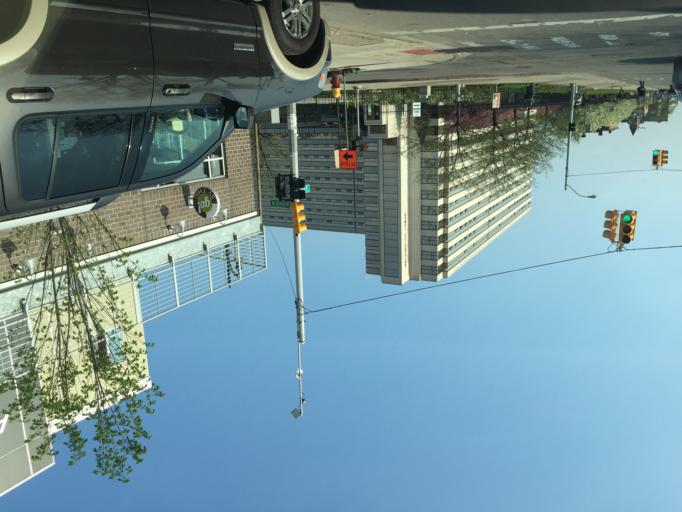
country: US
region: Michigan
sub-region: Wayne County
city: Detroit
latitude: 42.3514
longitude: -83.0640
